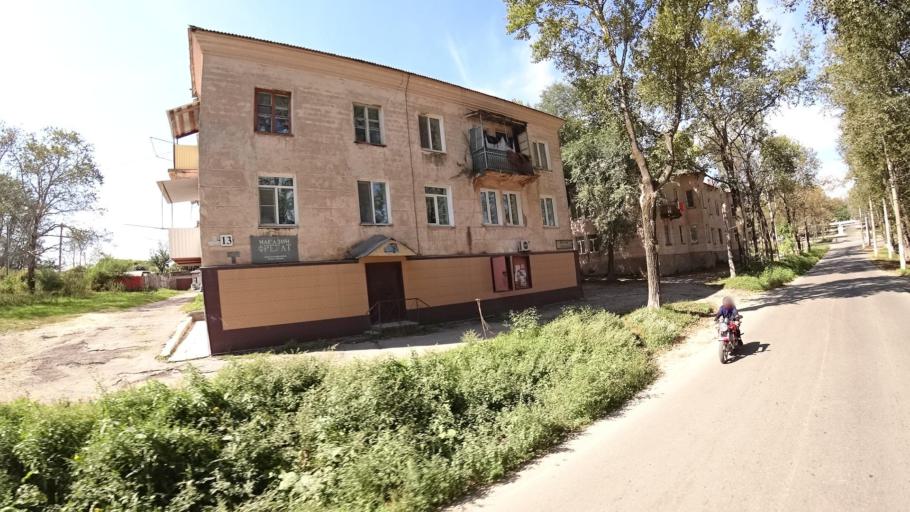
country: RU
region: Jewish Autonomous Oblast
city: Londoko
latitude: 49.0094
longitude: 131.8837
